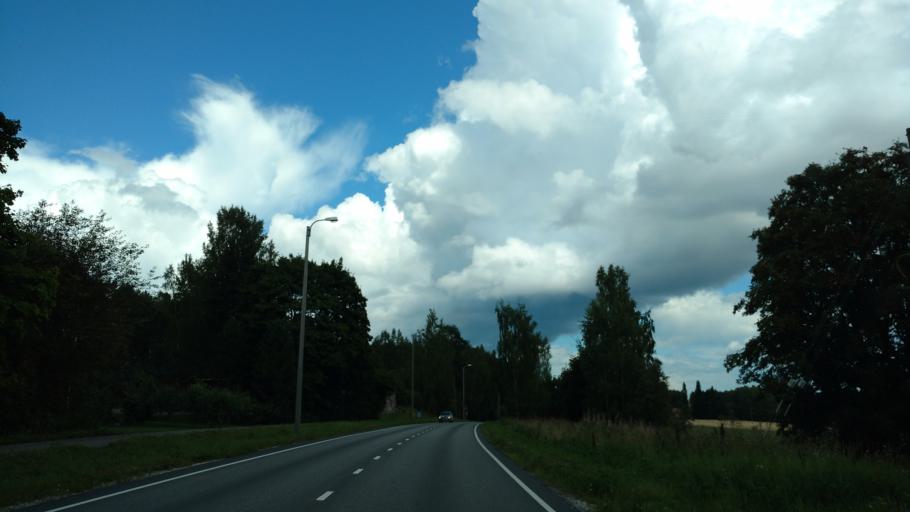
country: FI
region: Uusimaa
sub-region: Helsinki
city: Karjalohja
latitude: 60.2452
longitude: 23.7321
